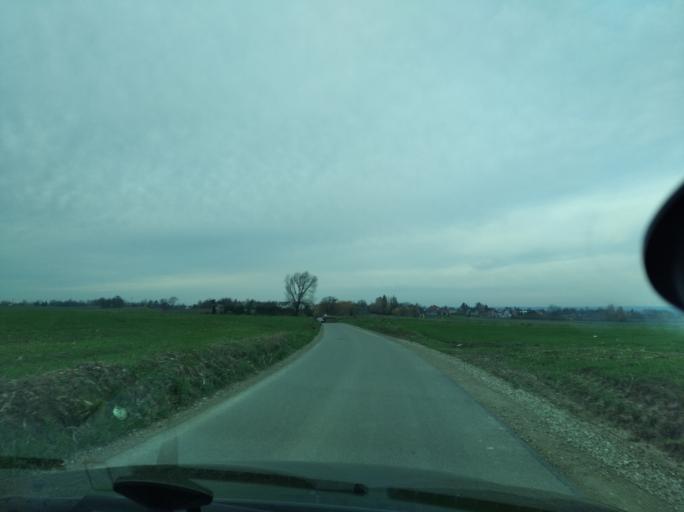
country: PL
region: Subcarpathian Voivodeship
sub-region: Powiat przeworski
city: Grzeska
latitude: 50.0692
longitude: 22.4609
